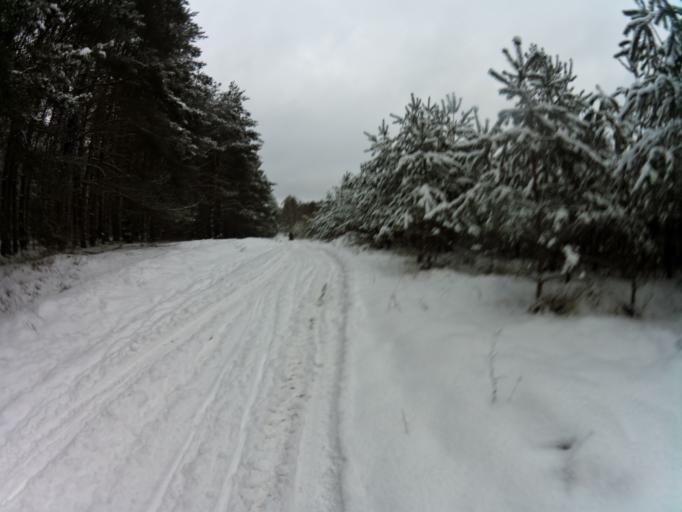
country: PL
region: West Pomeranian Voivodeship
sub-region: Powiat stargardzki
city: Dobrzany
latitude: 53.3577
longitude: 15.5148
